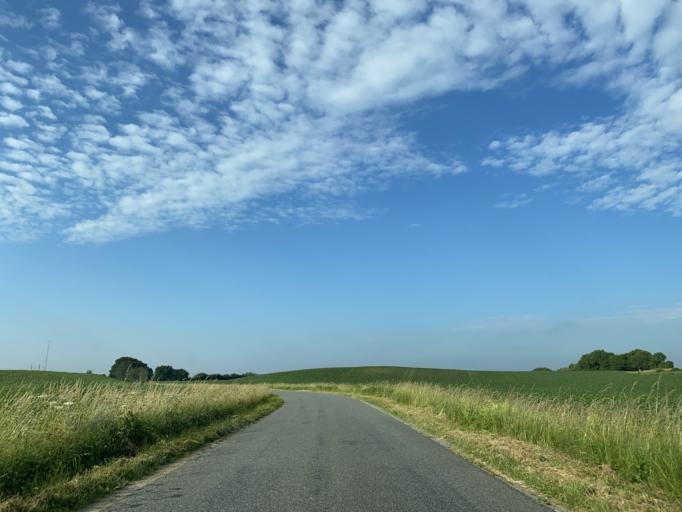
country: DK
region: South Denmark
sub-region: Haderslev Kommune
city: Haderslev
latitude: 55.1935
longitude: 9.4711
